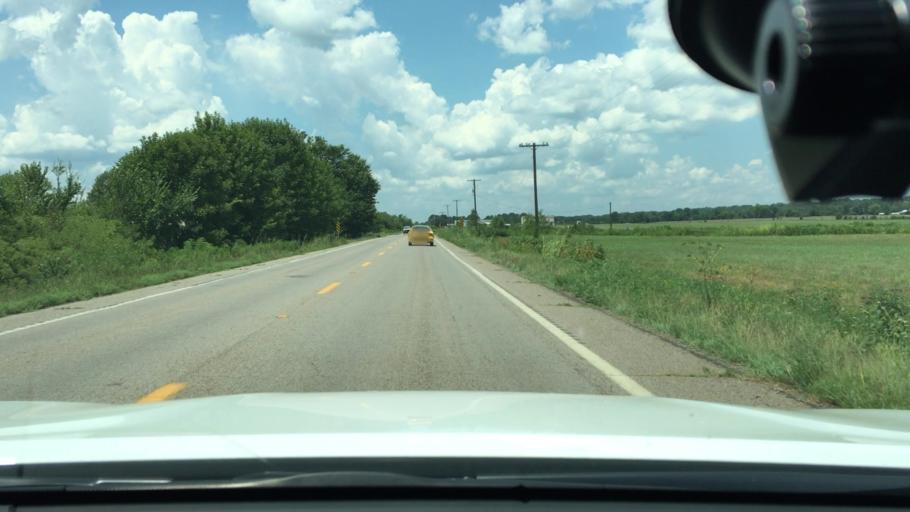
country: US
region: Arkansas
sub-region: Logan County
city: Booneville
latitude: 35.1477
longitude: -93.8575
